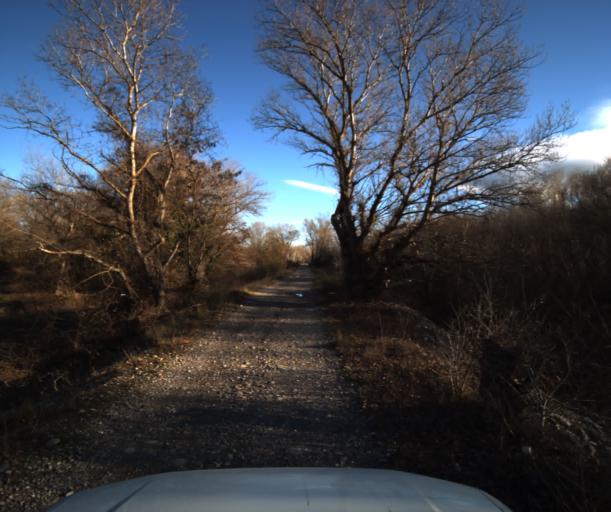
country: FR
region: Provence-Alpes-Cote d'Azur
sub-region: Departement du Vaucluse
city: Pertuis
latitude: 43.6745
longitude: 5.4709
